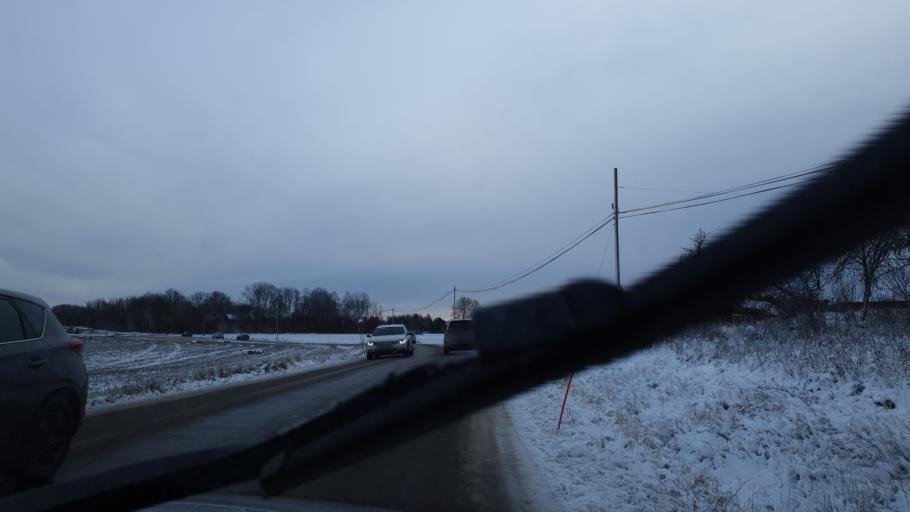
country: SE
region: Uppsala
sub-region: Habo Kommun
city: Balsta
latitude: 59.7087
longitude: 17.5681
